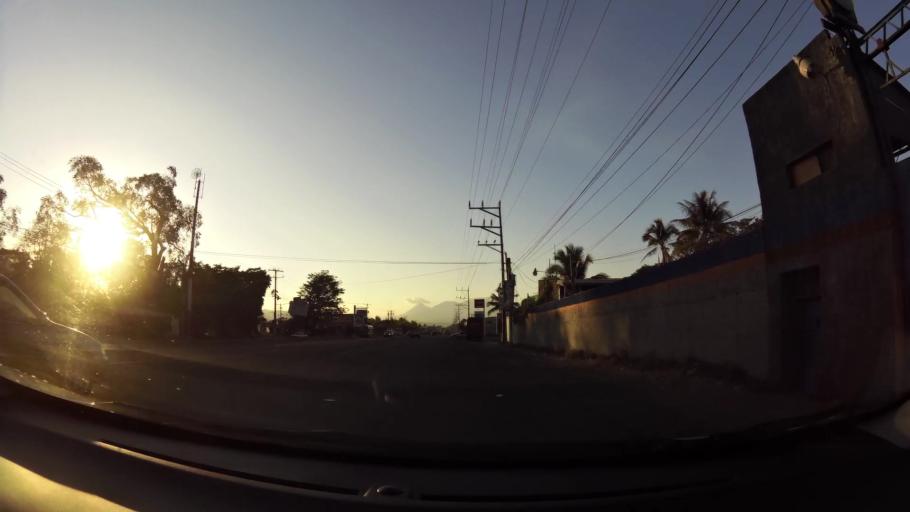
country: SV
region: Sonsonate
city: Armenia
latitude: 13.7348
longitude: -89.3913
